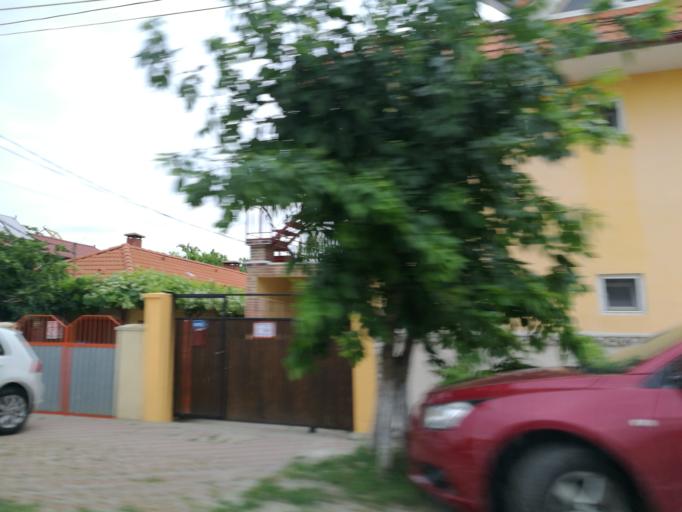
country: RO
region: Constanta
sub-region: Municipiul Mangalia
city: Mangalia
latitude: 43.7902
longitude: 28.5773
